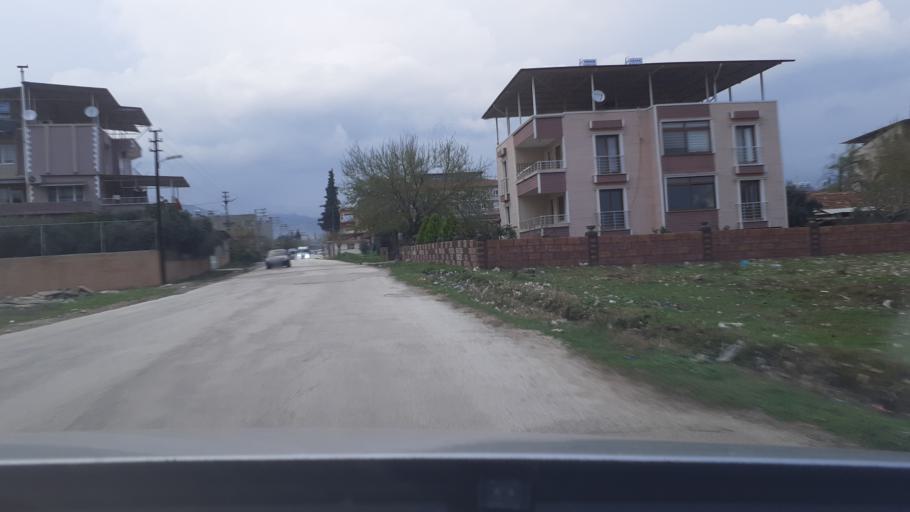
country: TR
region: Hatay
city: Kirikhan
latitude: 36.4856
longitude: 36.3556
